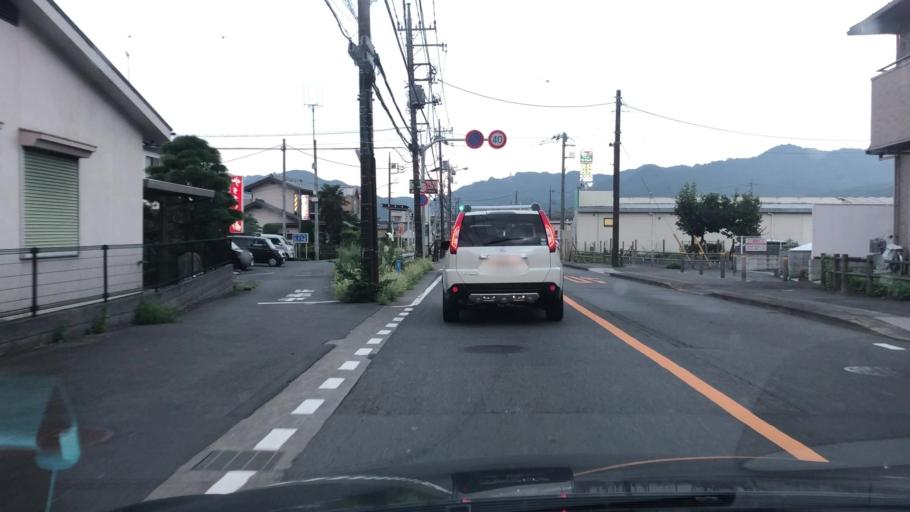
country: JP
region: Tokyo
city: Ome
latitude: 35.7907
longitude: 139.2203
